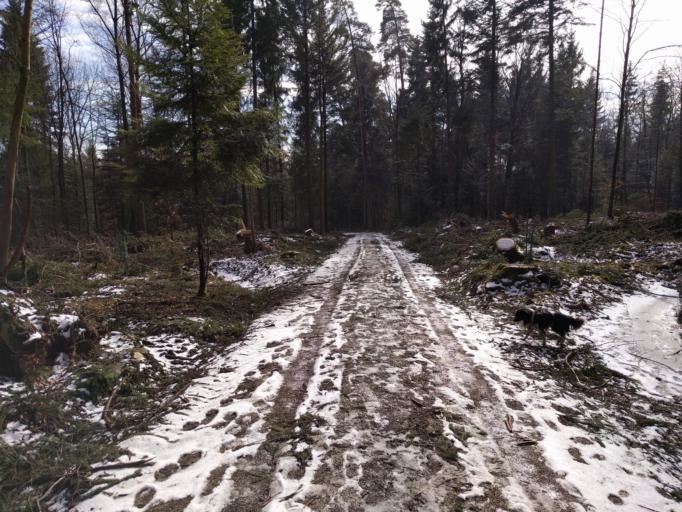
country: CH
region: Aargau
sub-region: Bezirk Aarau
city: Kuttigen
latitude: 47.4101
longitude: 8.0365
